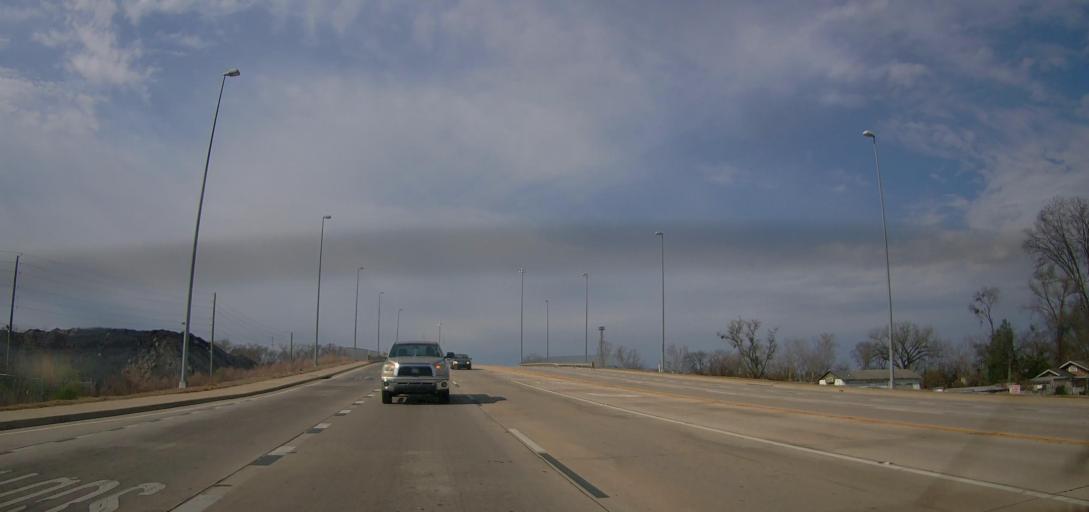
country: US
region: Alabama
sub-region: Jefferson County
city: Birmingham
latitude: 33.5245
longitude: -86.8500
